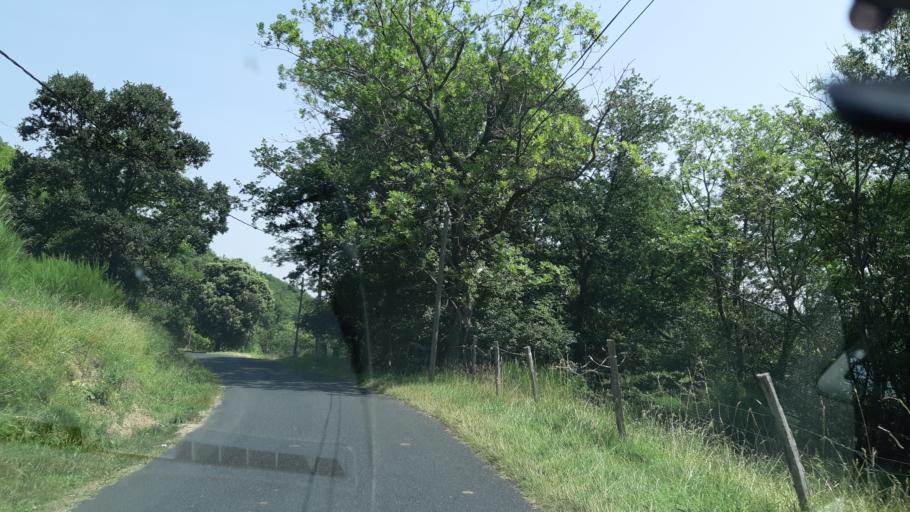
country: FR
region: Languedoc-Roussillon
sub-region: Departement des Pyrenees-Orientales
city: els Banys d'Arles
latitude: 42.5063
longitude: 2.6361
